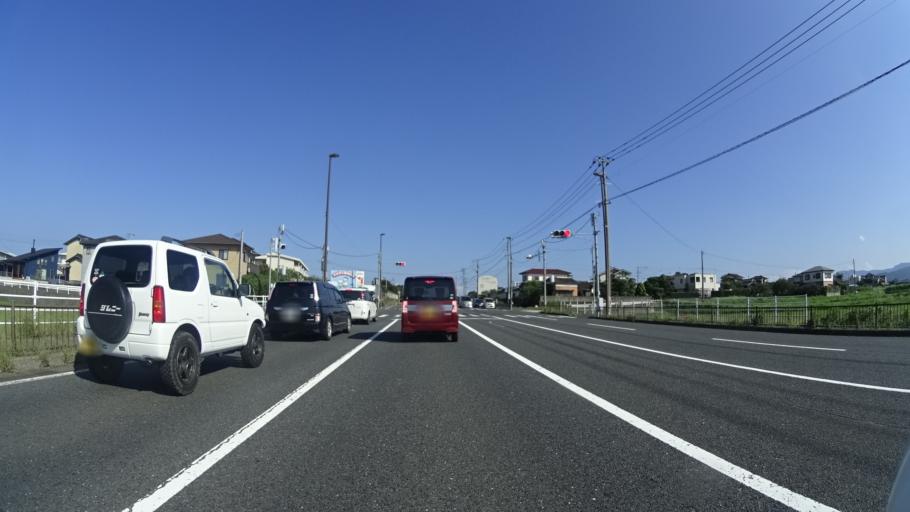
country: JP
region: Fukuoka
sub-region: Buzen-shi
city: Buzen
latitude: 33.6040
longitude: 131.1219
